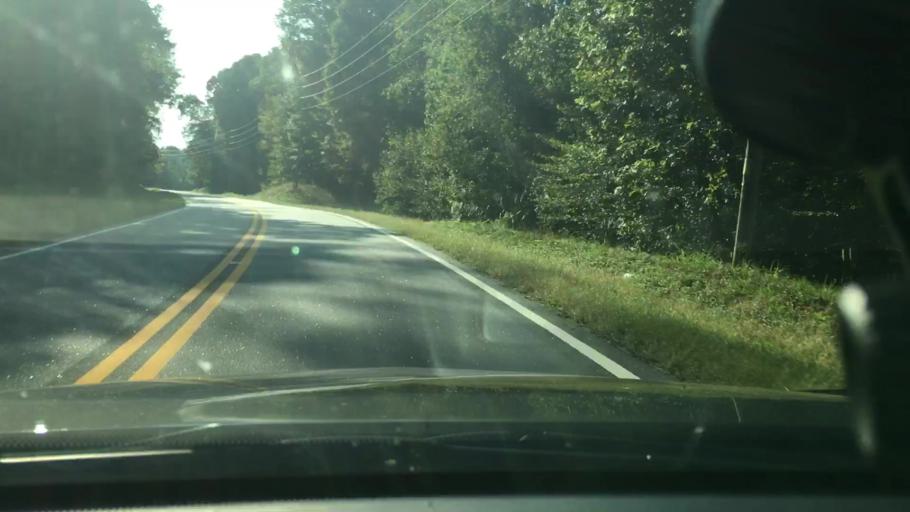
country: US
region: North Carolina
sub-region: Rutherford County
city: Rutherfordton
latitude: 35.3305
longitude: -82.0564
